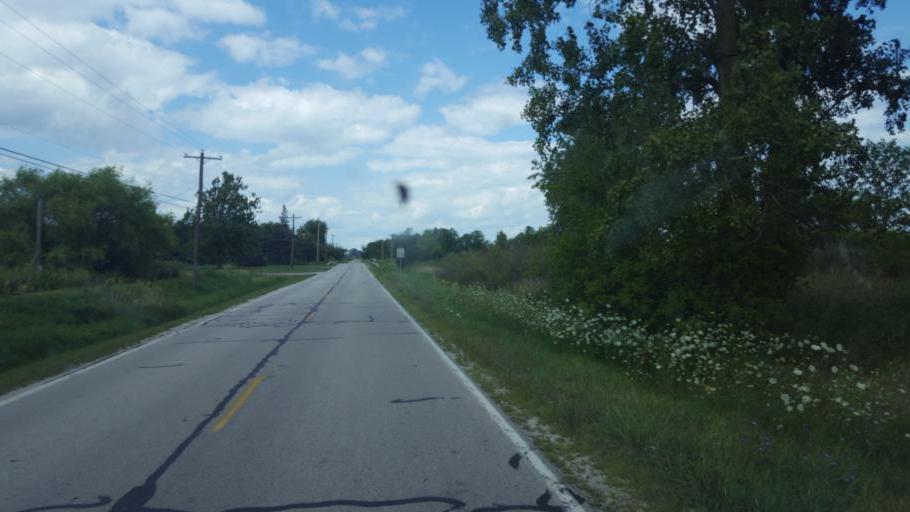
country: US
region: Ohio
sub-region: Lucas County
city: Curtice
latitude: 41.6224
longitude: -83.2794
